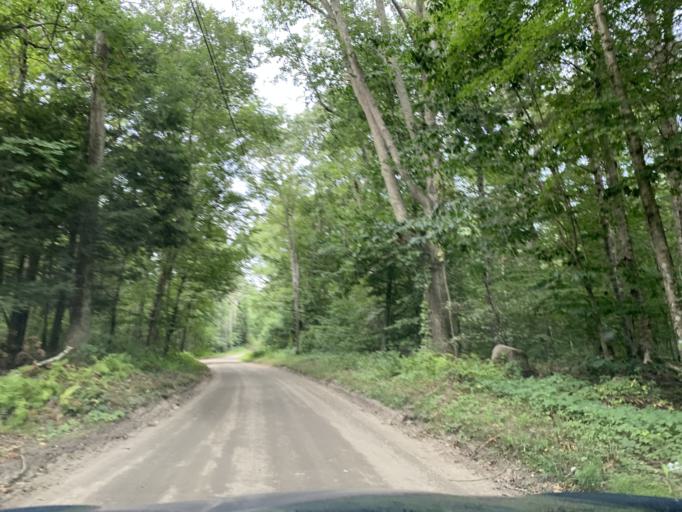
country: US
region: Rhode Island
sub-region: Kent County
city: West Greenwich
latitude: 41.5784
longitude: -71.6438
